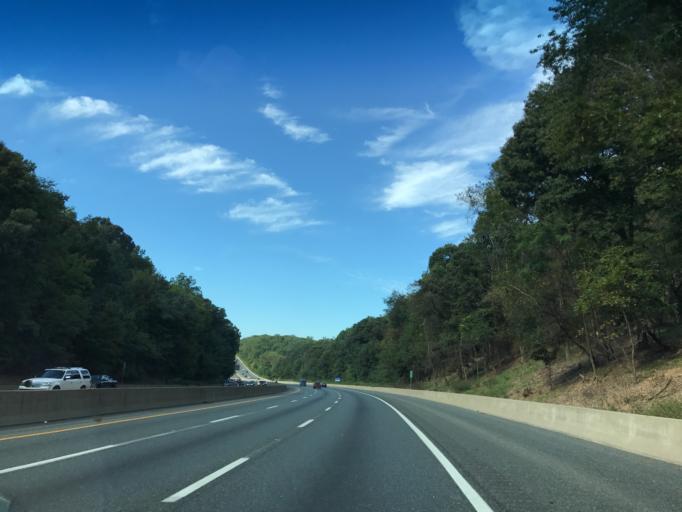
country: US
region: Maryland
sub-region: Anne Arundel County
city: Riva
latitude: 38.9837
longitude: -76.5996
